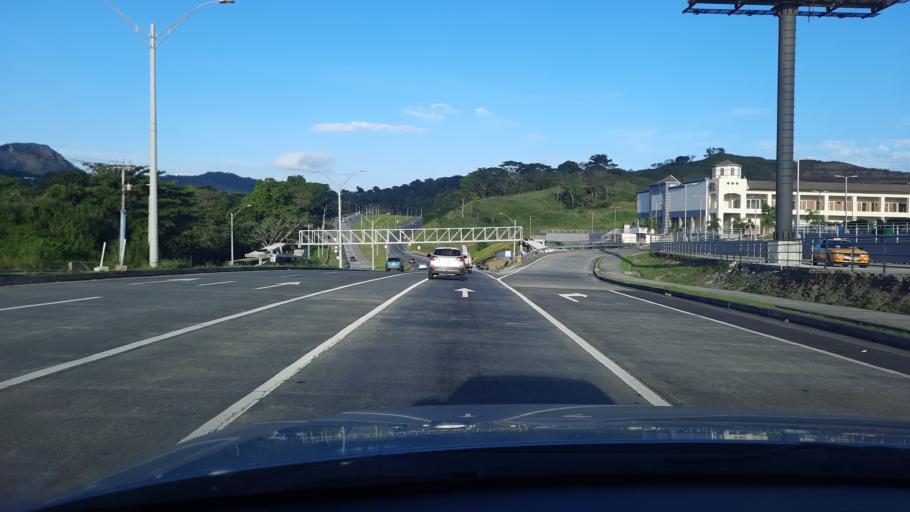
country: PA
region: Panama
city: Las Cumbres
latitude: 9.1023
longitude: -79.5214
